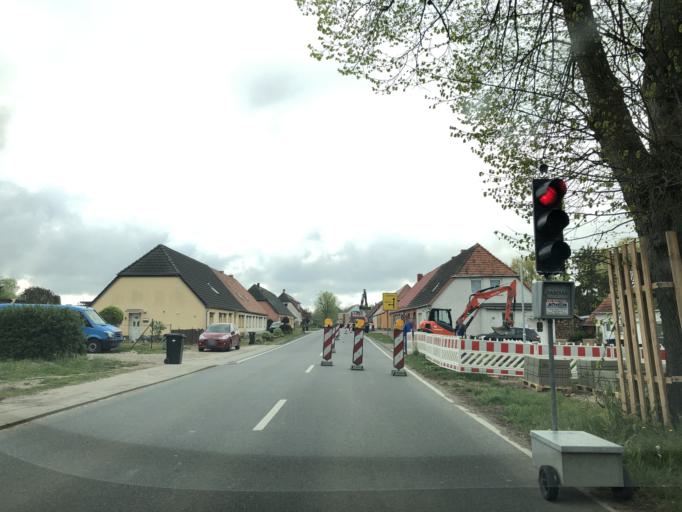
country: DE
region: Mecklenburg-Vorpommern
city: Guestrow
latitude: 53.7161
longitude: 12.1380
